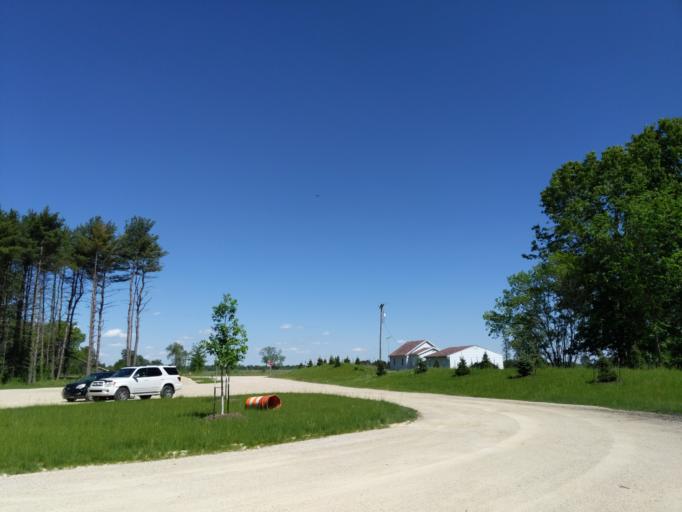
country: US
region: Michigan
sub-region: Jackson County
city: Michigan Center
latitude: 42.3210
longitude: -84.3404
